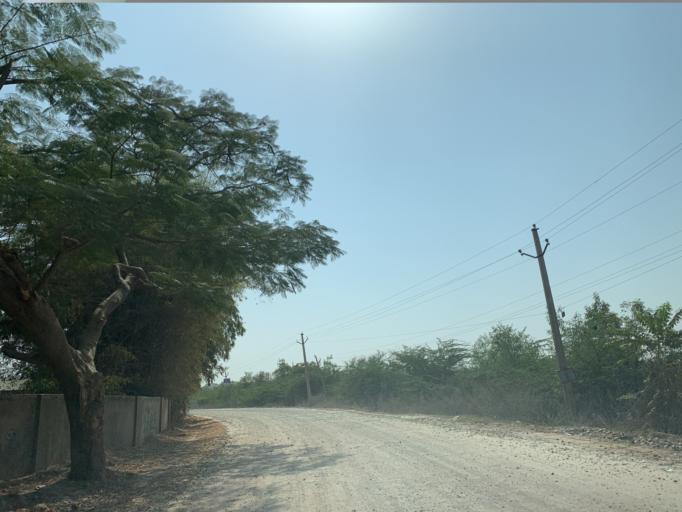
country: IN
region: Telangana
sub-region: Rangareddi
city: Sriramnagar
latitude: 17.3307
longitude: 78.2967
